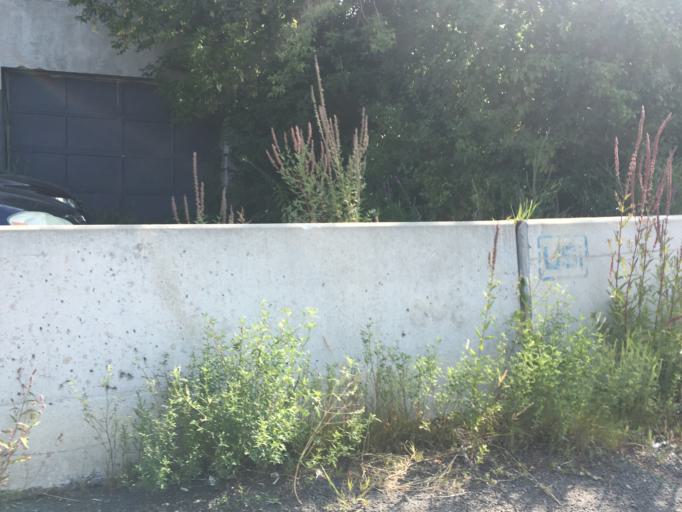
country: CA
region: Ontario
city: Ottawa
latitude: 45.3761
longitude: -75.6671
